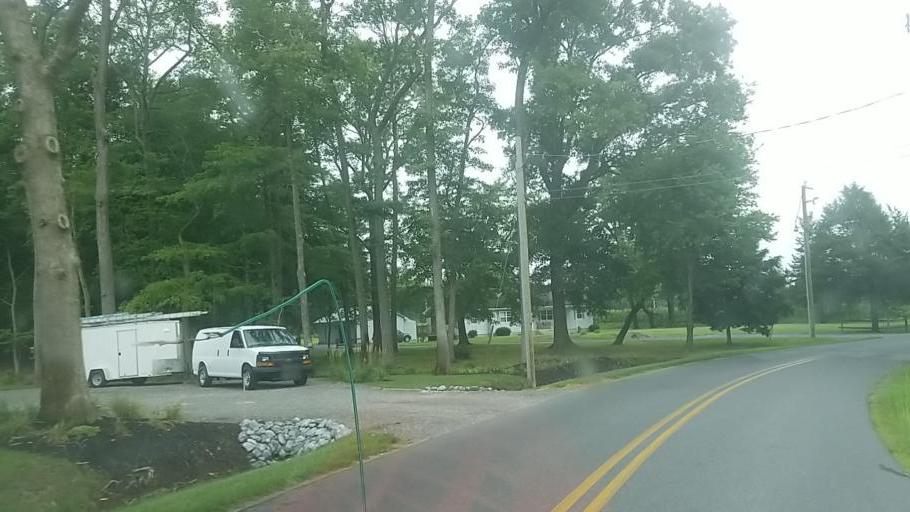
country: US
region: Delaware
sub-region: Sussex County
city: Selbyville
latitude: 38.4427
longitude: -75.2234
